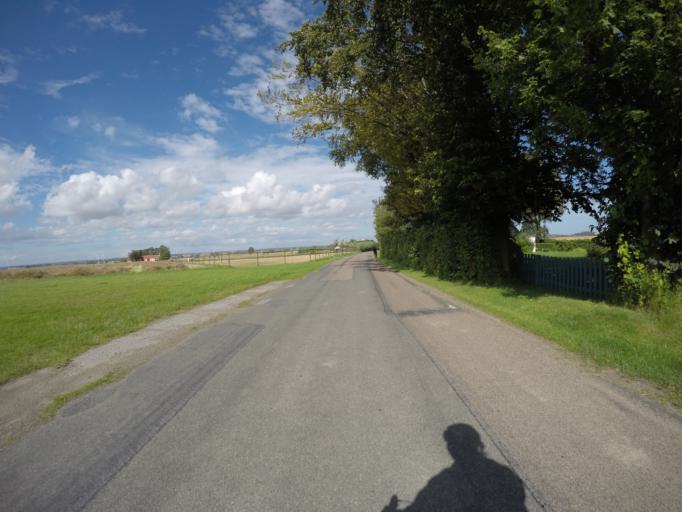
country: SE
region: Skane
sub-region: Simrishamns Kommun
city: Simrishamn
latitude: 55.4915
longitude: 14.1951
